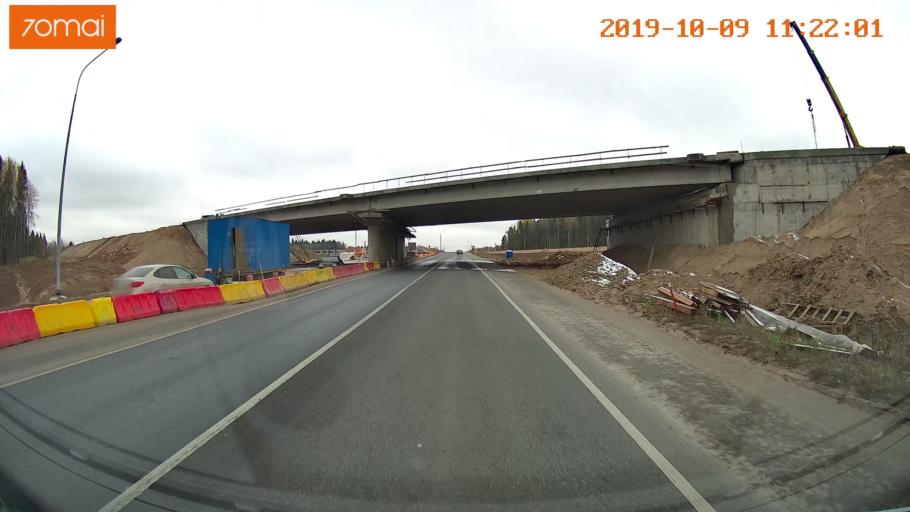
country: RU
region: Vologda
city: Vologda
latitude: 59.1350
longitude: 39.9544
